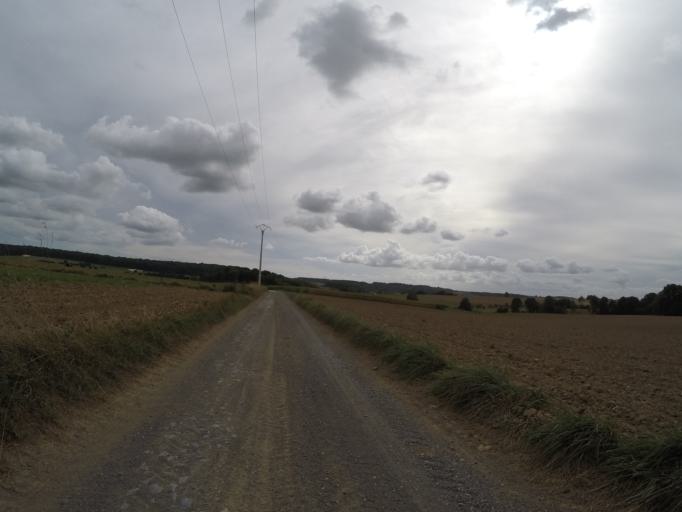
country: BE
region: Wallonia
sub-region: Province de Namur
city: Dinant
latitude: 50.2908
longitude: 4.9861
